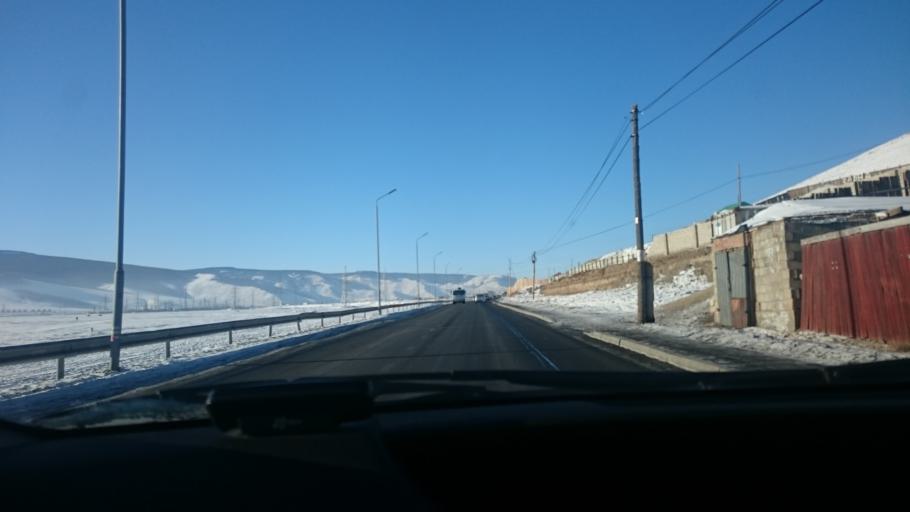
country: MN
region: Ulaanbaatar
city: Ulaanbaatar
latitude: 47.9150
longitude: 107.0534
